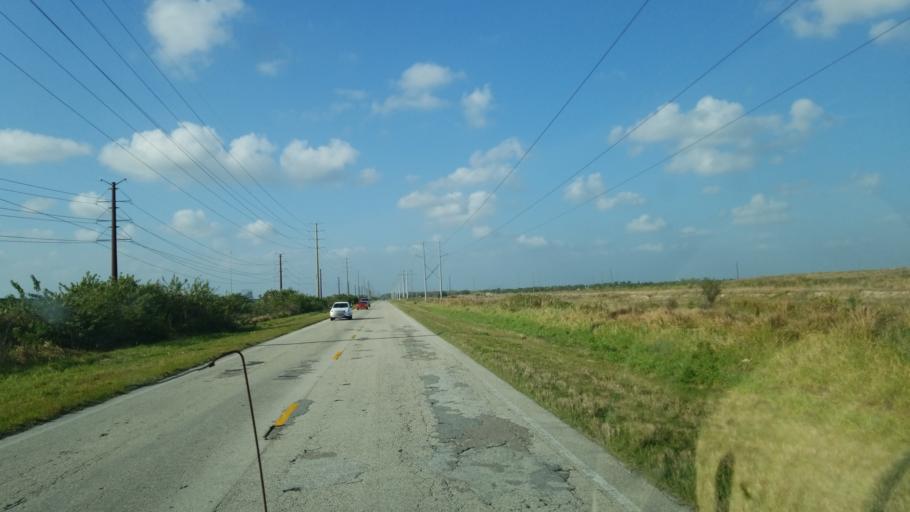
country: US
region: Florida
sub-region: Hardee County
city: Wauchula
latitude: 27.5669
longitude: -81.9345
